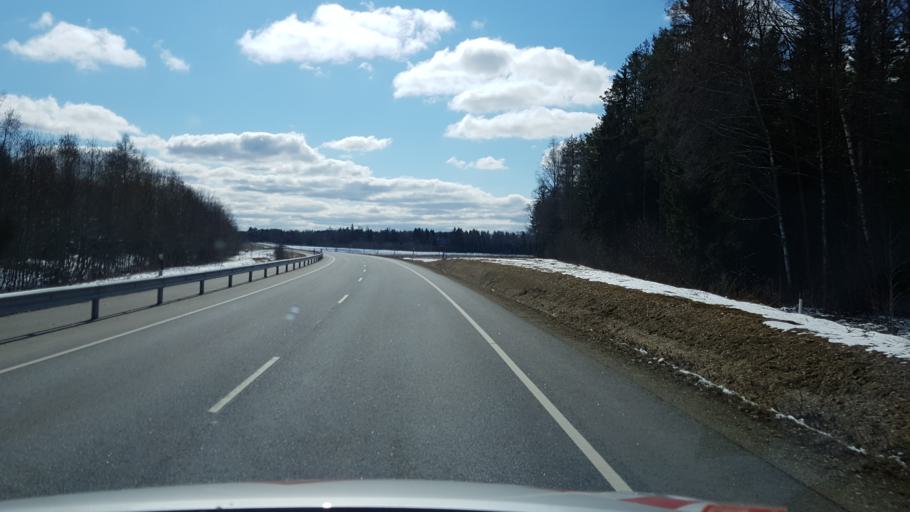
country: EE
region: Laeaene-Virumaa
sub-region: Kadrina vald
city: Kadrina
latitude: 59.4683
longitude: 25.9984
